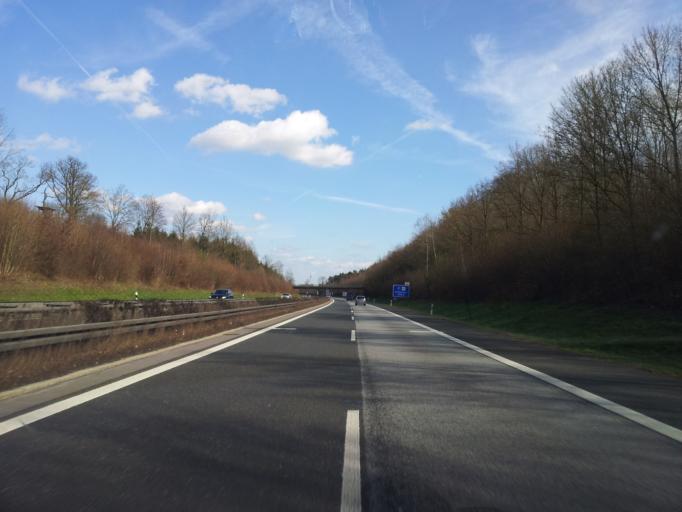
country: DE
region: Bavaria
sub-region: Regierungsbezirk Unterfranken
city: Donnersdorf
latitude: 50.0034
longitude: 10.3999
